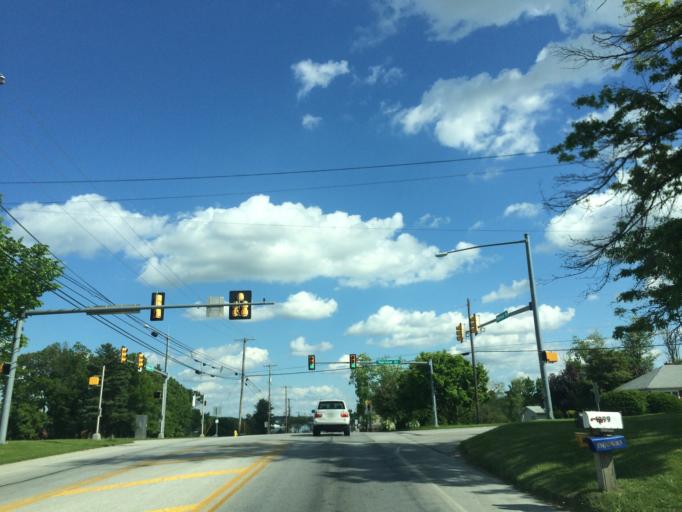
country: US
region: Pennsylvania
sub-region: York County
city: Parkville
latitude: 39.7609
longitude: -76.9583
